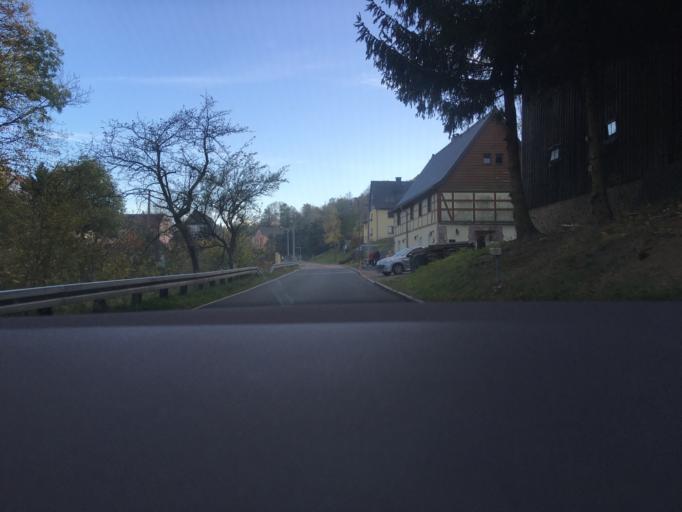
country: DE
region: Saxony
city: Glashutte
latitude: 50.8420
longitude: 13.7989
